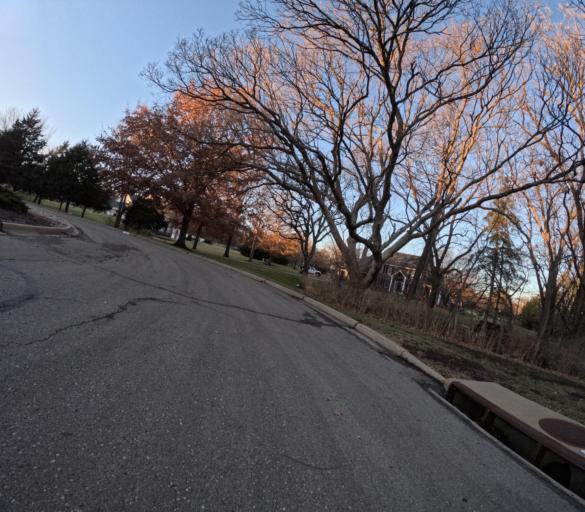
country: US
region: Kansas
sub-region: Riley County
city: Manhattan
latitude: 39.1941
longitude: -96.6329
